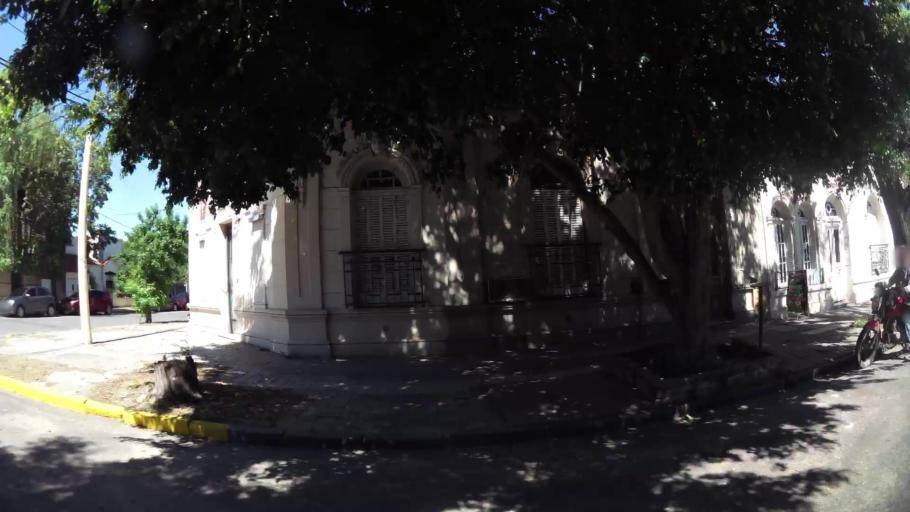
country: AR
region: Santa Fe
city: Santa Fe de la Vera Cruz
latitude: -31.6427
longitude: -60.6892
